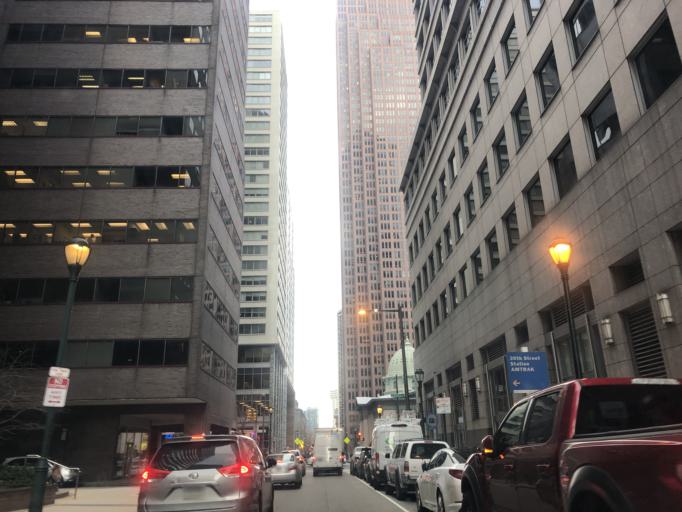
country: US
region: Pennsylvania
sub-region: Philadelphia County
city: Philadelphia
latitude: 39.9536
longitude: -75.1700
